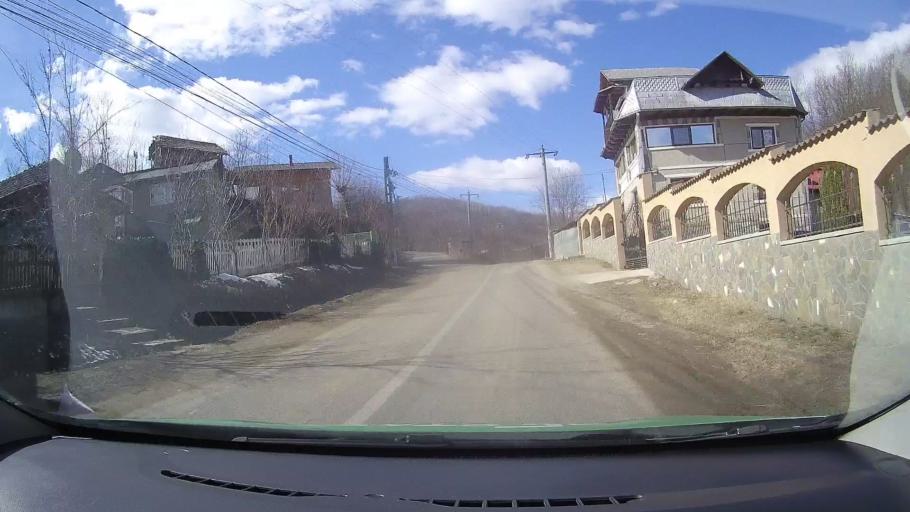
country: RO
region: Dambovita
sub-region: Comuna Glodeni
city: Laculete
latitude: 45.0208
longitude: 25.4365
